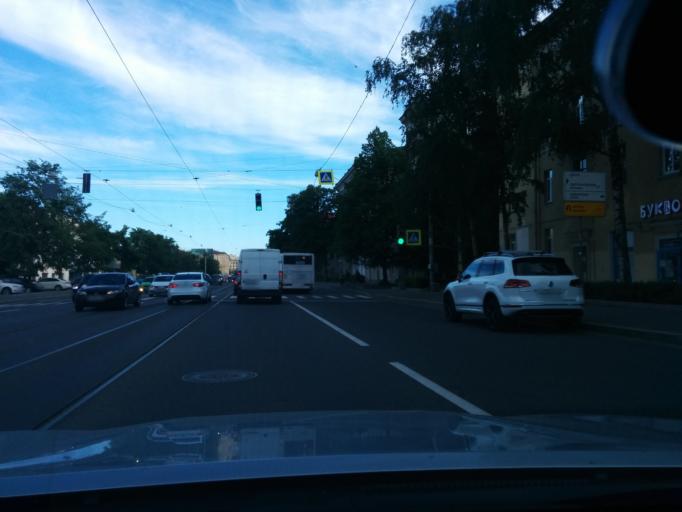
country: RU
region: Leningrad
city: Svetlanovskiy
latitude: 60.0092
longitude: 30.3254
